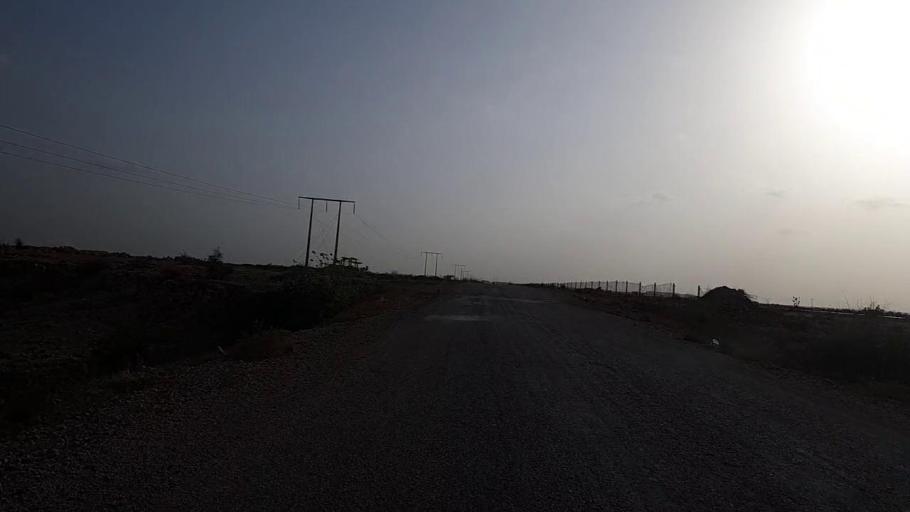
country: PK
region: Sindh
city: Thatta
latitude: 25.1921
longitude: 67.8561
